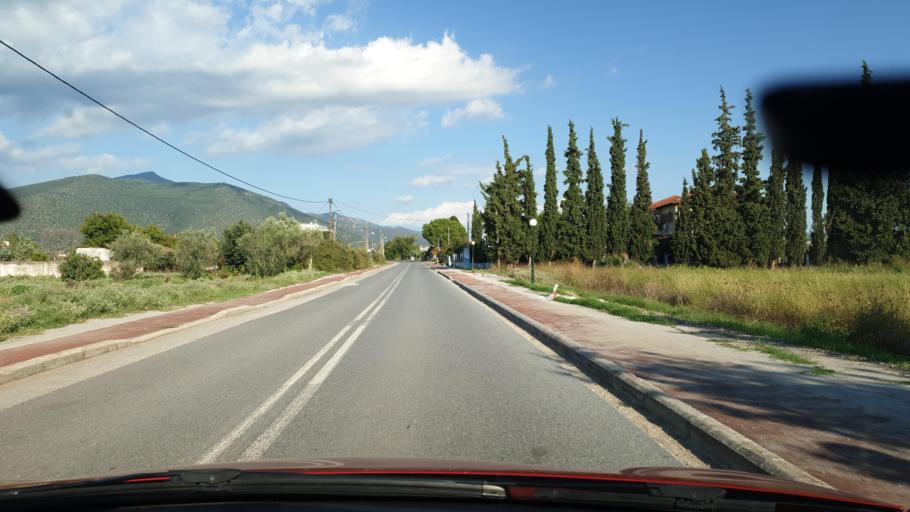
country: GR
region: Central Macedonia
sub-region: Nomos Thessalonikis
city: Vasilika
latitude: 40.4806
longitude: 23.1255
